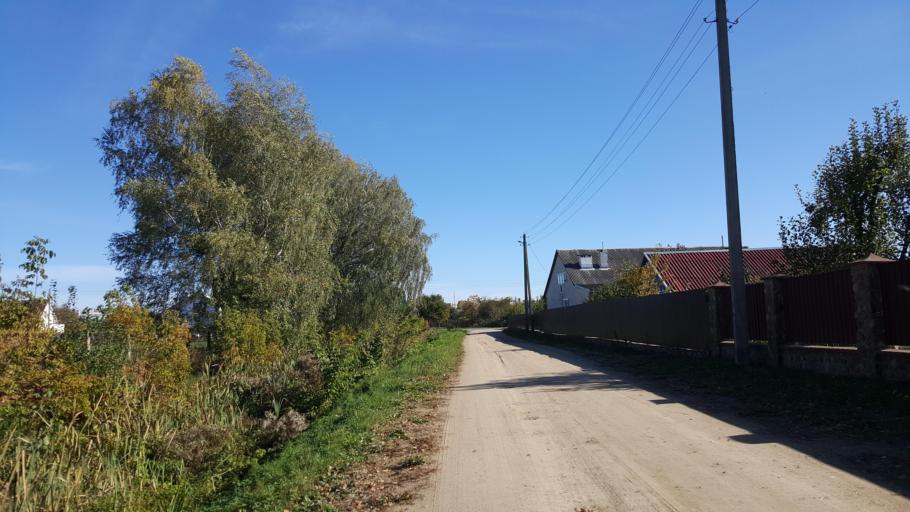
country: BY
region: Brest
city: Kamyanyets
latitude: 52.3974
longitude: 23.8111
